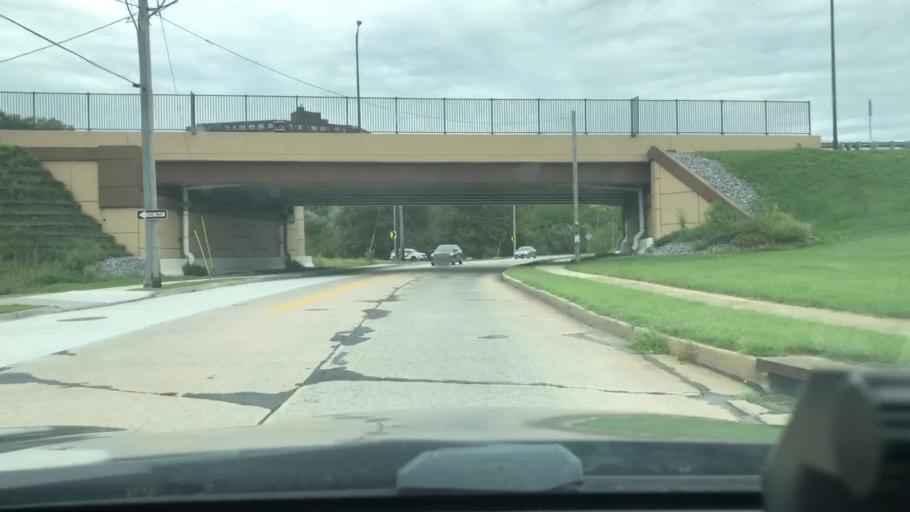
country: US
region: Pennsylvania
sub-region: Lehigh County
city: Allentown
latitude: 40.5920
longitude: -75.4835
